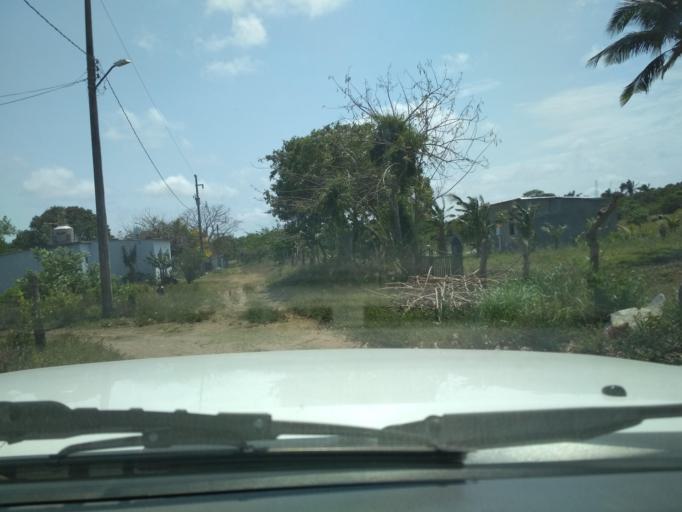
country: MX
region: Veracruz
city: Anton Lizardo
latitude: 19.0025
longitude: -95.9924
